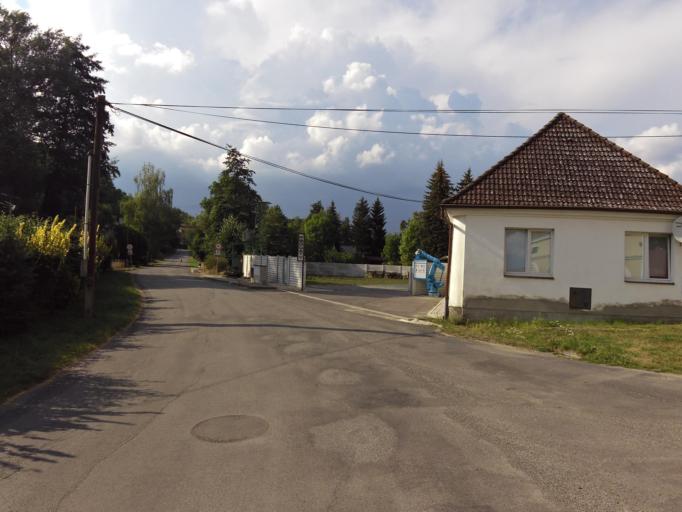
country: CZ
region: Central Bohemia
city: Mnichovo Hradiste
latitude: 50.5248
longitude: 14.9458
